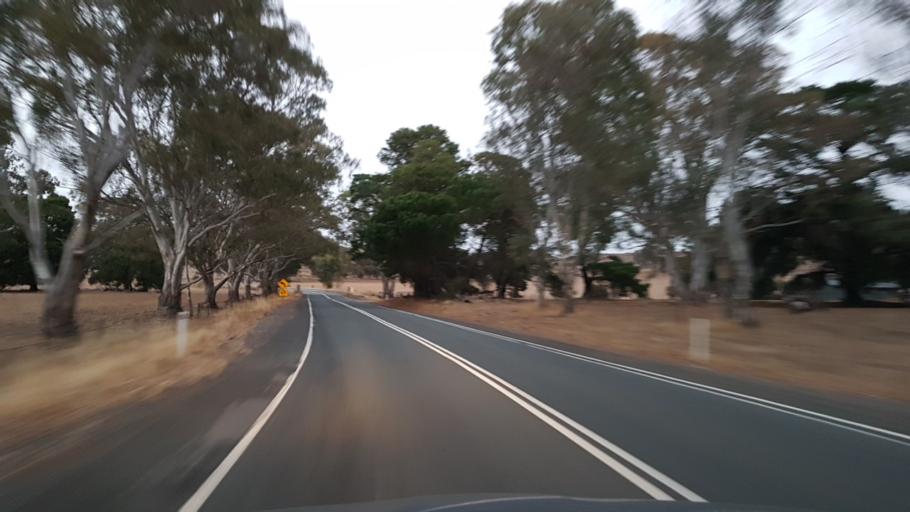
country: AU
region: South Australia
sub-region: Mount Barker
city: Nairne
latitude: -35.0396
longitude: 138.9868
